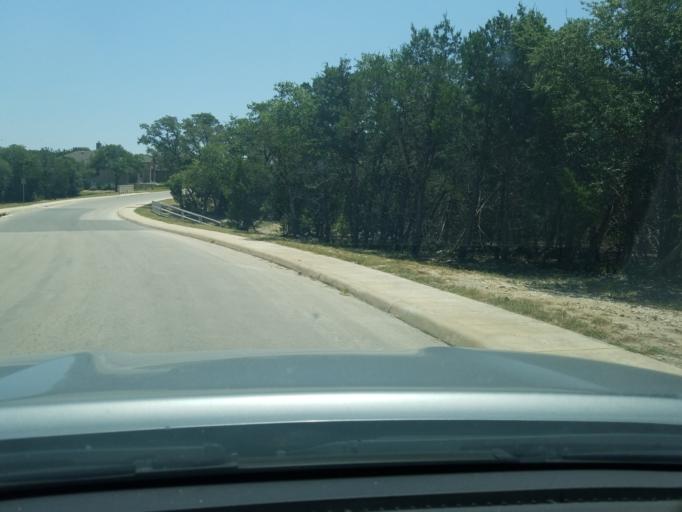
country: US
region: Texas
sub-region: Bexar County
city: Timberwood Park
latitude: 29.7100
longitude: -98.5063
